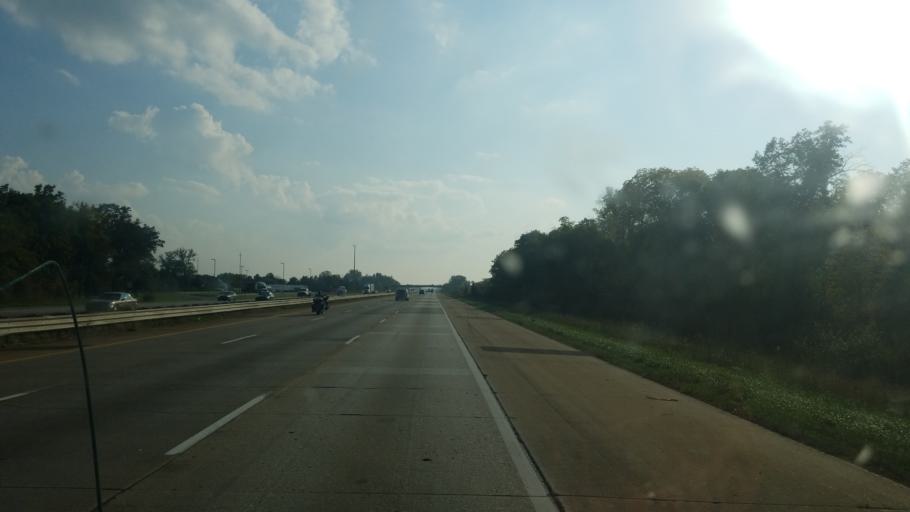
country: US
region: Michigan
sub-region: Monroe County
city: South Monroe
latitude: 41.8675
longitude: -83.4039
